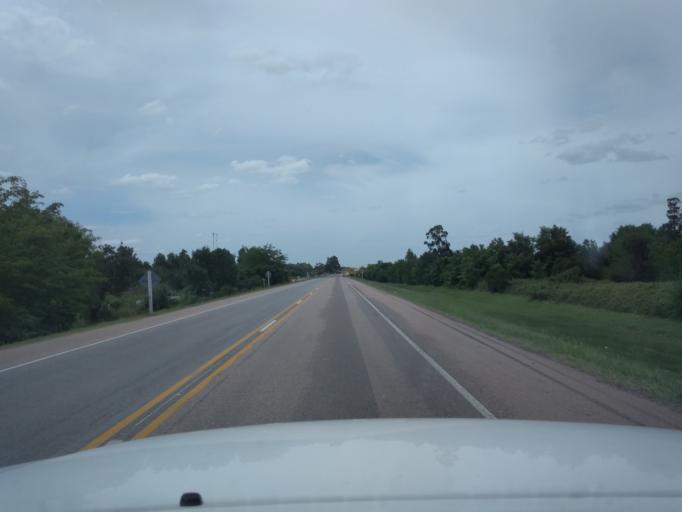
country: UY
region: Canelones
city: Canelones
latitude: -34.5016
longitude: -56.2817
